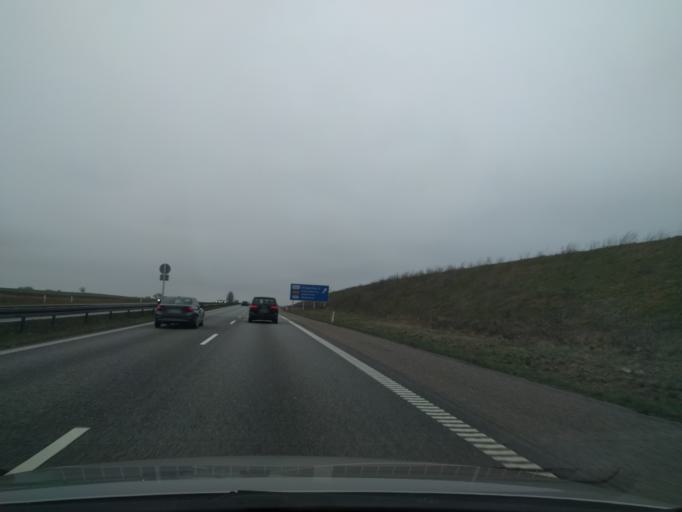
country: DK
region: Zealand
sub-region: Soro Kommune
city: Soro
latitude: 55.4473
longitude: 11.5378
